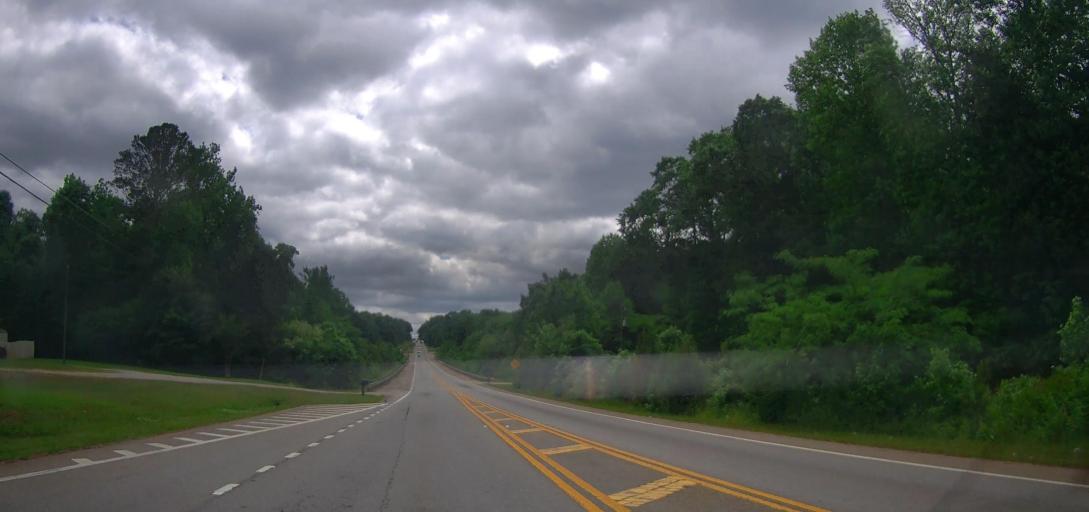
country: US
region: Georgia
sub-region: Henry County
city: Stockbridge
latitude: 33.5528
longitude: -84.1765
